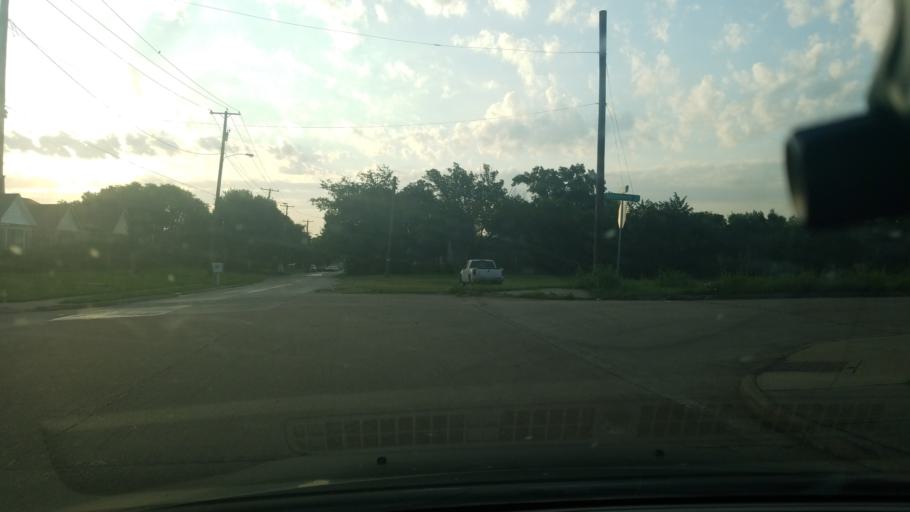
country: US
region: Texas
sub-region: Dallas County
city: Balch Springs
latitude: 32.7277
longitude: -96.6511
